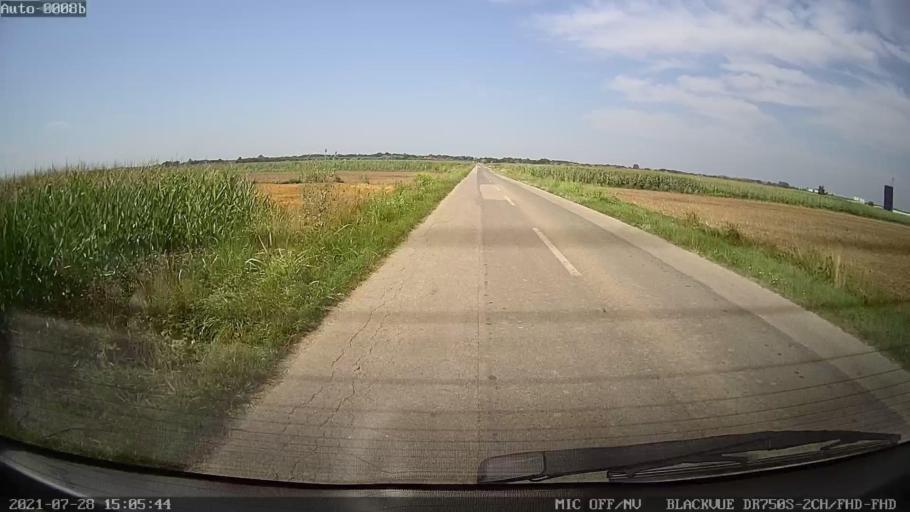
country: HR
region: Varazdinska
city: Jalzabet
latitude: 46.2663
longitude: 16.4348
